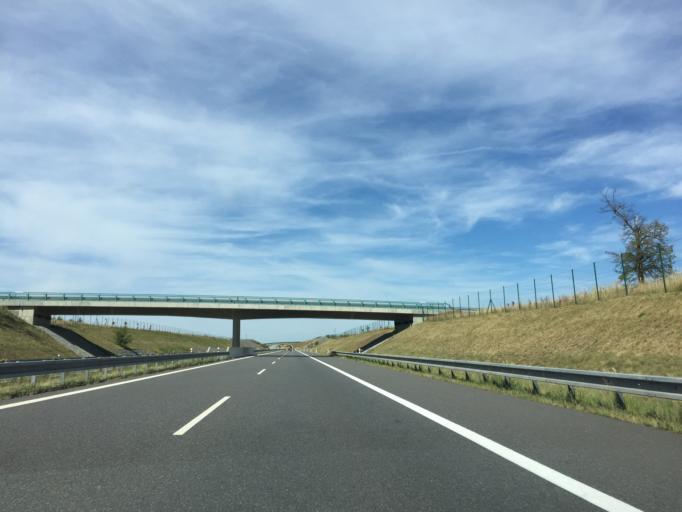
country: CZ
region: Jihocesky
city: Sobeslav
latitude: 49.2987
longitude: 14.7365
